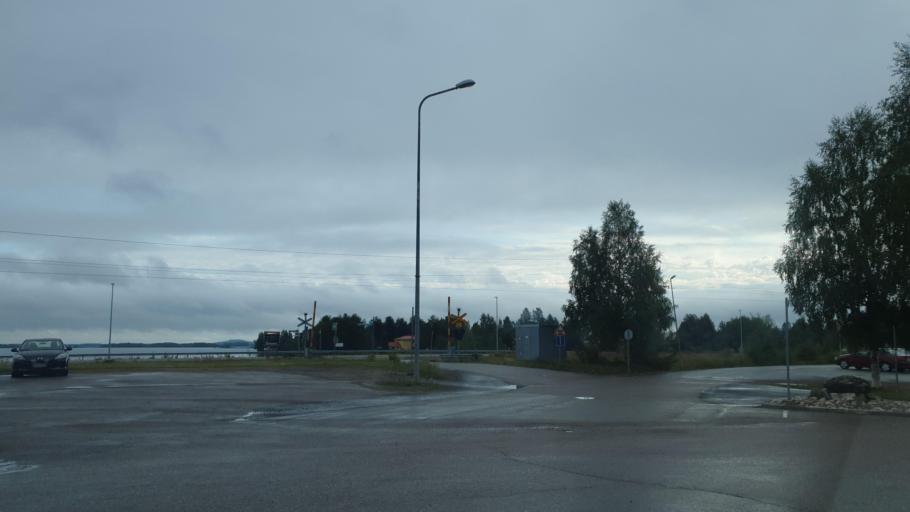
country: FI
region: Lapland
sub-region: Itae-Lappi
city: Kemijaervi
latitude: 66.7171
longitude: 27.4267
